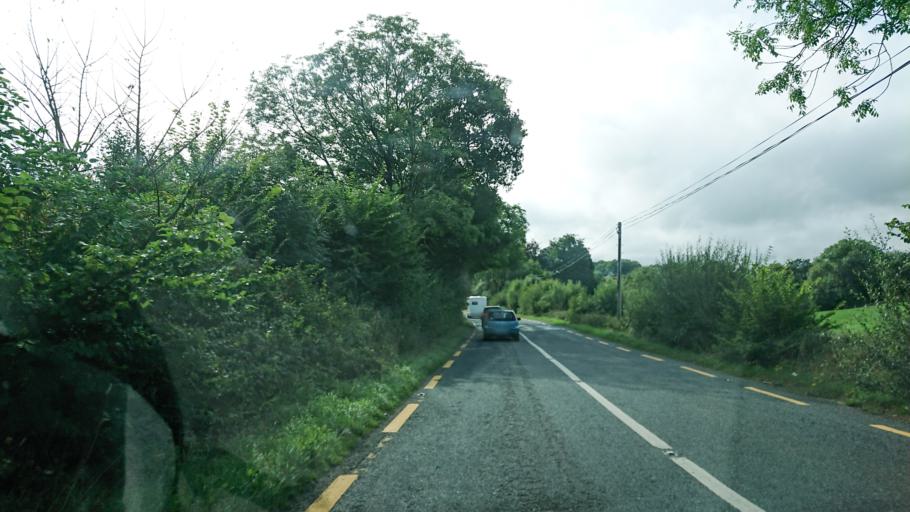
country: IE
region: Munster
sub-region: County Cork
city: Millstreet
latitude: 52.0860
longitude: -9.1740
